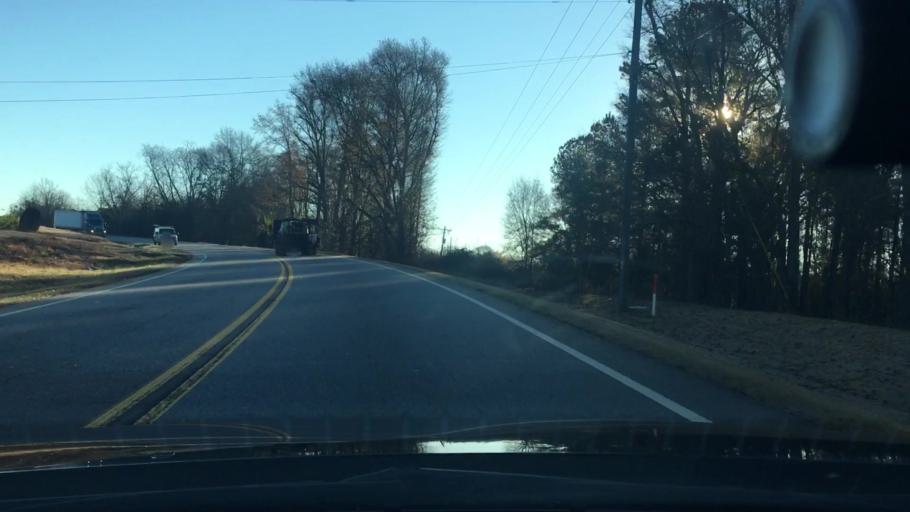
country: US
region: Georgia
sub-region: Spalding County
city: Experiment
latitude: 33.2384
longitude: -84.4052
